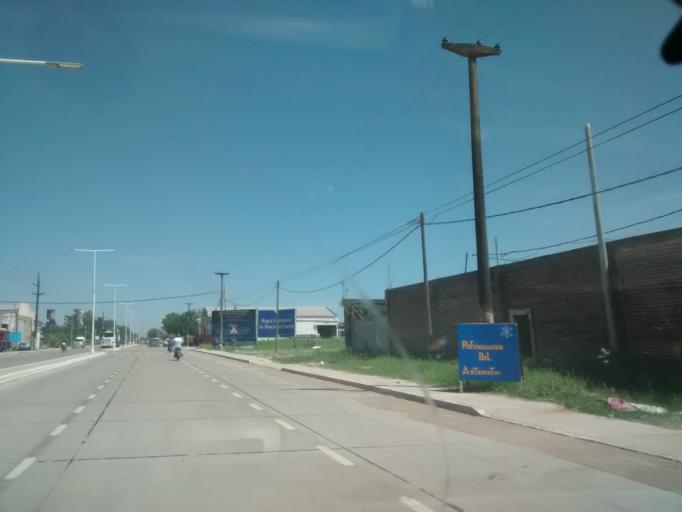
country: AR
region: Chaco
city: Fontana
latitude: -27.4329
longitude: -59.0214
